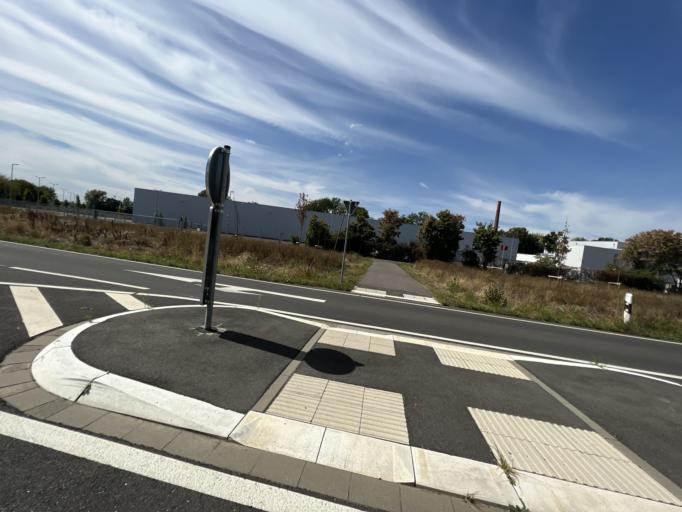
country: DE
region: North Rhine-Westphalia
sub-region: Regierungsbezirk Koln
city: Niederzier
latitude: 50.8437
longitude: 6.4358
